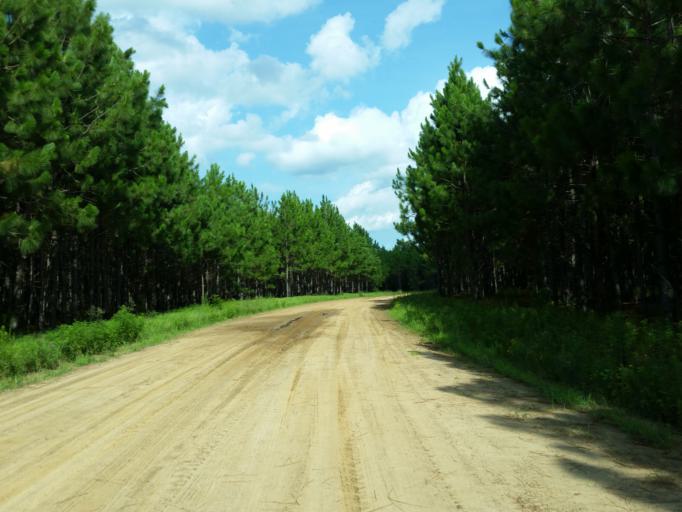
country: US
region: Georgia
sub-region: Lee County
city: Leesburg
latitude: 31.7664
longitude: -84.0349
